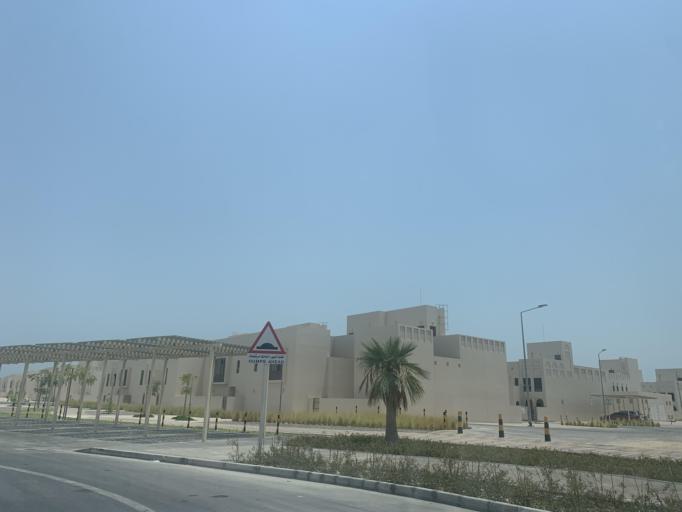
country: BH
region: Muharraq
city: Al Hadd
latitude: 26.2363
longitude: 50.6662
